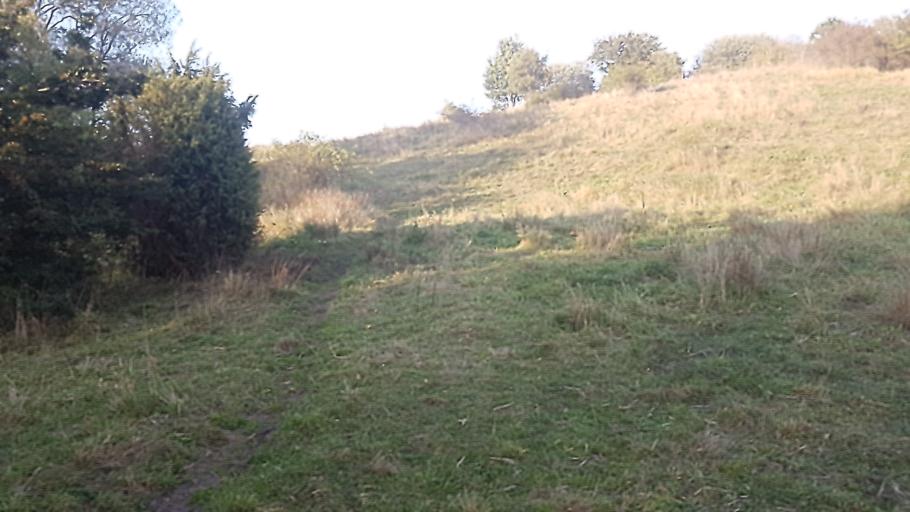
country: SE
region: Kalmar
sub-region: Kalmar Kommun
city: Rinkabyholm
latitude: 56.6597
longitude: 16.3054
